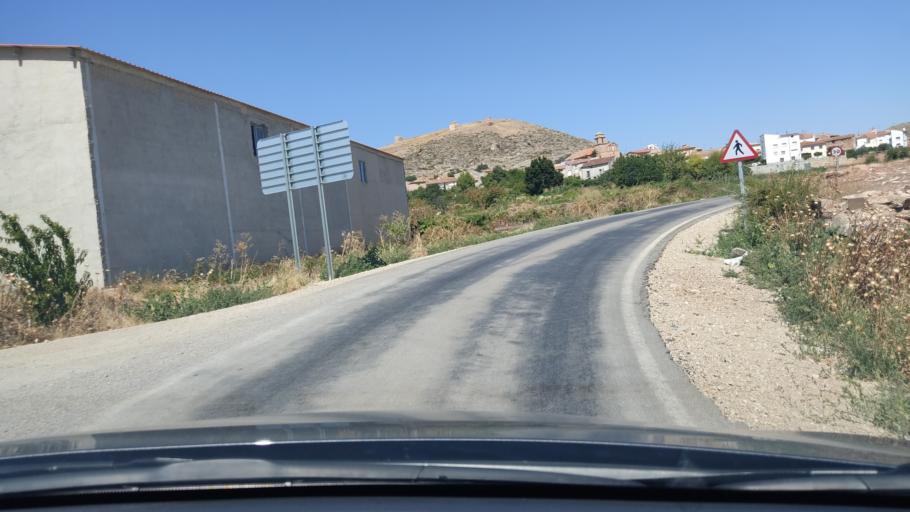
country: ES
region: Aragon
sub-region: Provincia de Teruel
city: Monforte de Moyuela
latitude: 41.0516
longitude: -1.0123
